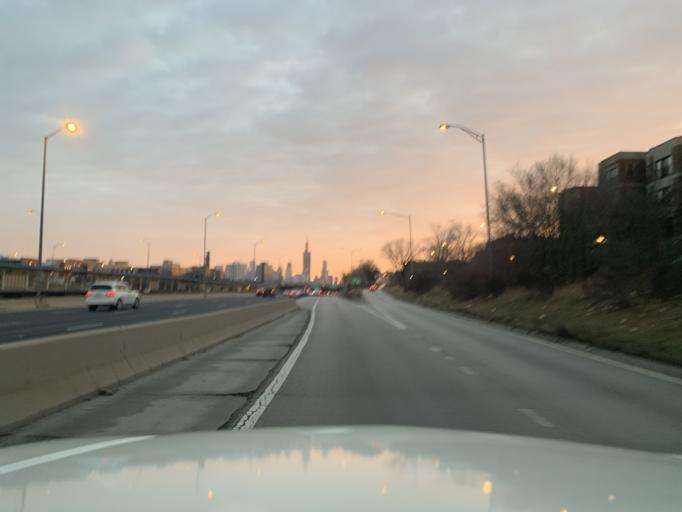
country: US
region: Illinois
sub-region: Cook County
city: Chicago
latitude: 41.8751
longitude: -87.6902
